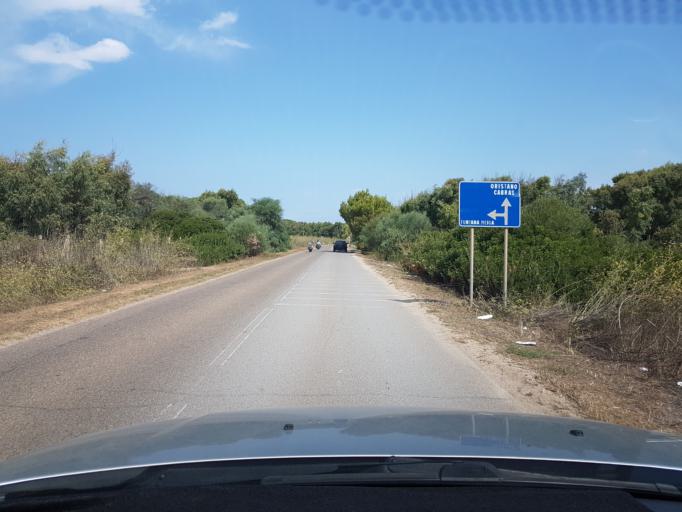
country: IT
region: Sardinia
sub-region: Provincia di Oristano
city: Cabras
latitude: 39.8881
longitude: 8.4359
